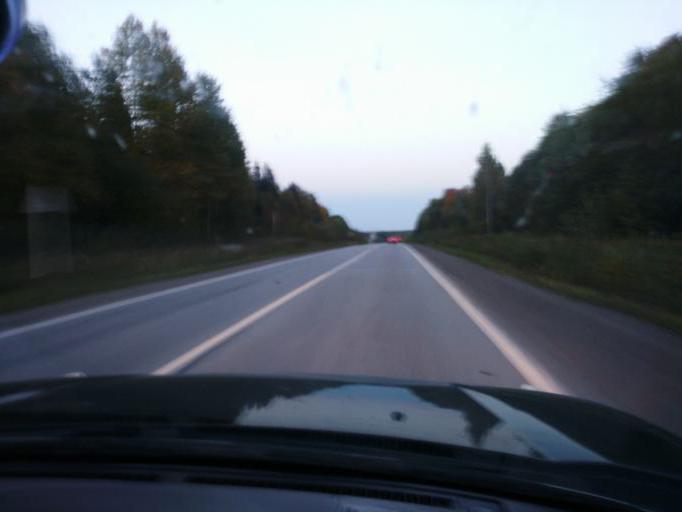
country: RU
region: Perm
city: Verkhnechusovskiye Gorodki
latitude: 58.2609
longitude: 56.9798
